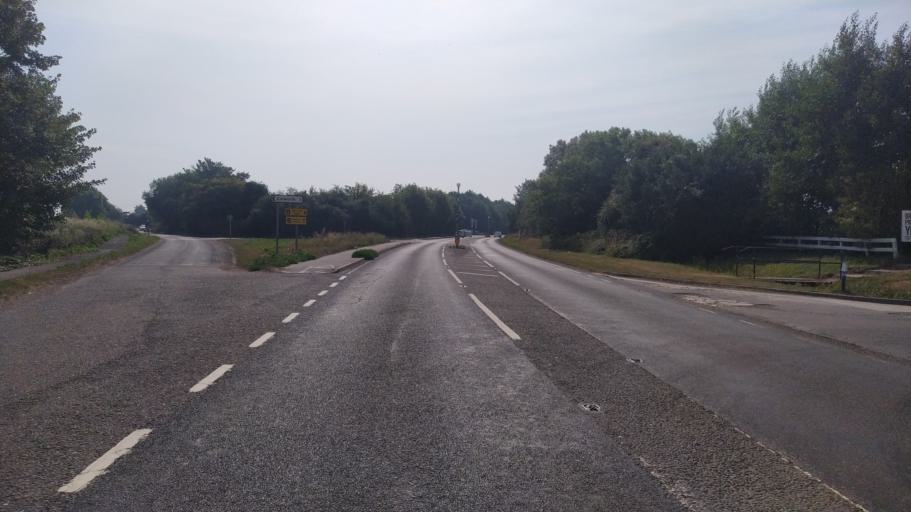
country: GB
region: England
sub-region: West Sussex
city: Boxgrove
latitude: 50.8209
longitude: -0.7186
